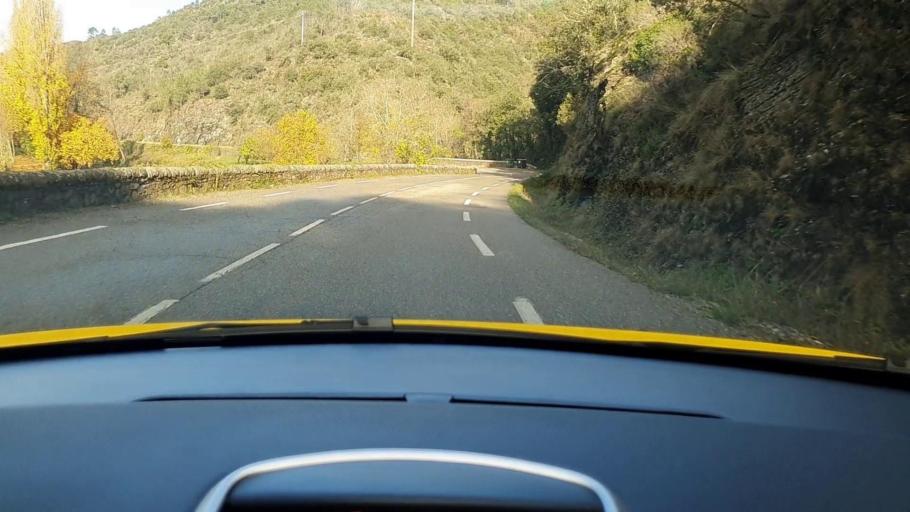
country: FR
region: Languedoc-Roussillon
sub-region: Departement du Gard
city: Valleraugue
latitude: 44.1446
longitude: 3.6995
